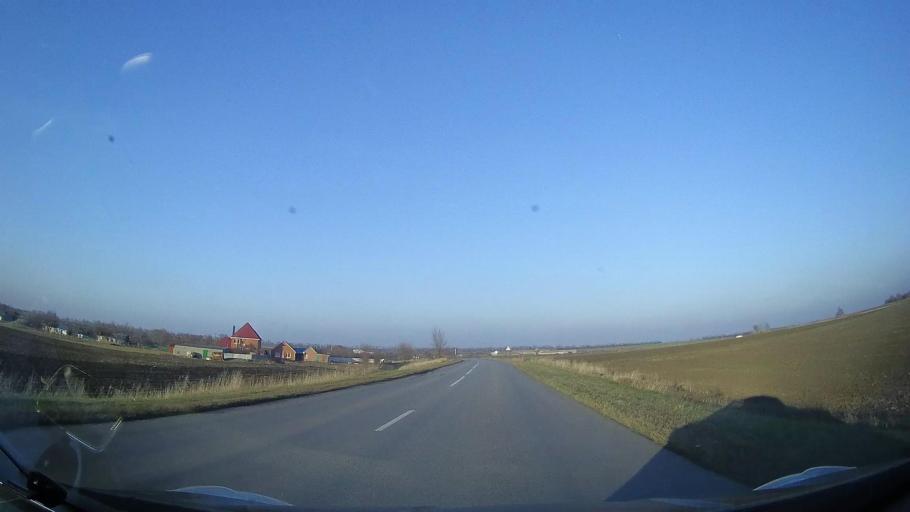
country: RU
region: Rostov
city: Kirovskaya
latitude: 47.0287
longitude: 39.9800
